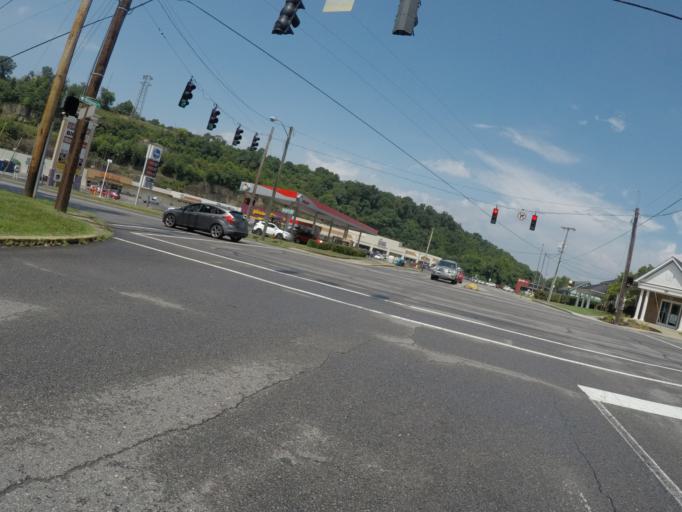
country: US
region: Kentucky
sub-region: Boyd County
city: Ashland
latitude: 38.4772
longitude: -82.6469
